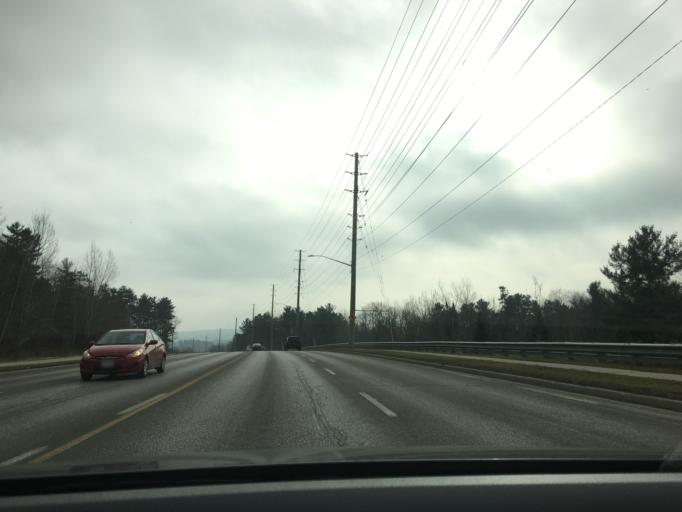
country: CA
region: Ontario
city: Barrie
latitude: 44.3848
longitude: -79.7284
